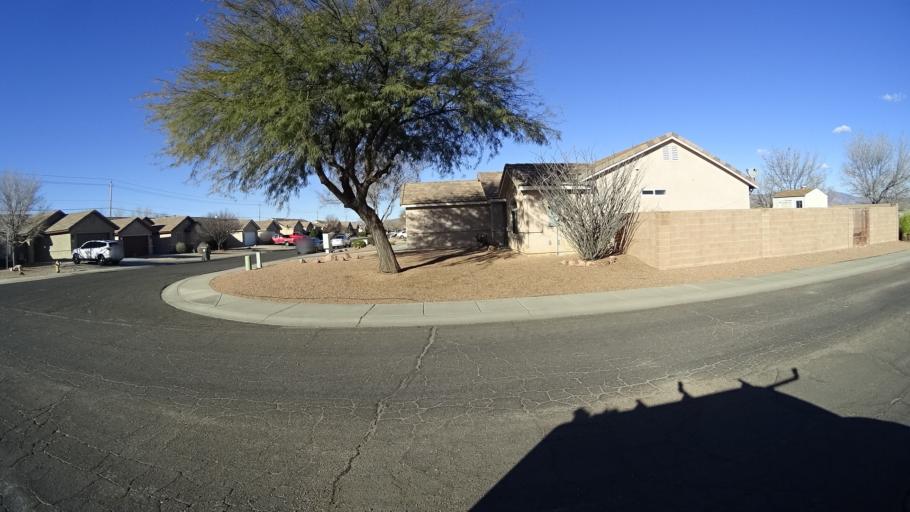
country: US
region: Arizona
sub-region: Mohave County
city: New Kingman-Butler
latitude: 35.2255
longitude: -113.9848
